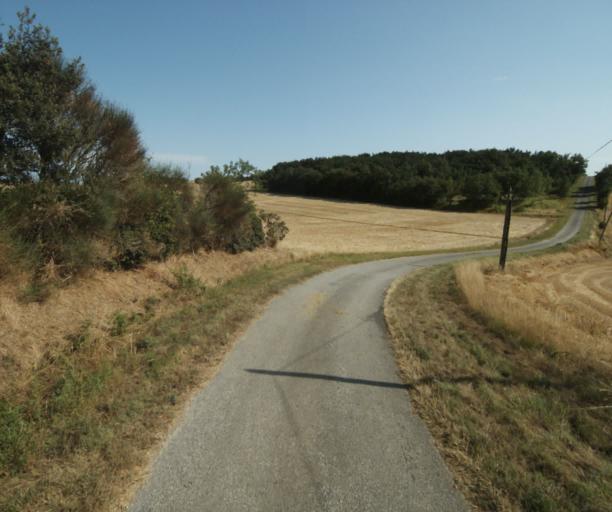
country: FR
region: Midi-Pyrenees
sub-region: Departement de la Haute-Garonne
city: Saint-Felix-Lauragais
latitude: 43.4248
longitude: 1.8321
